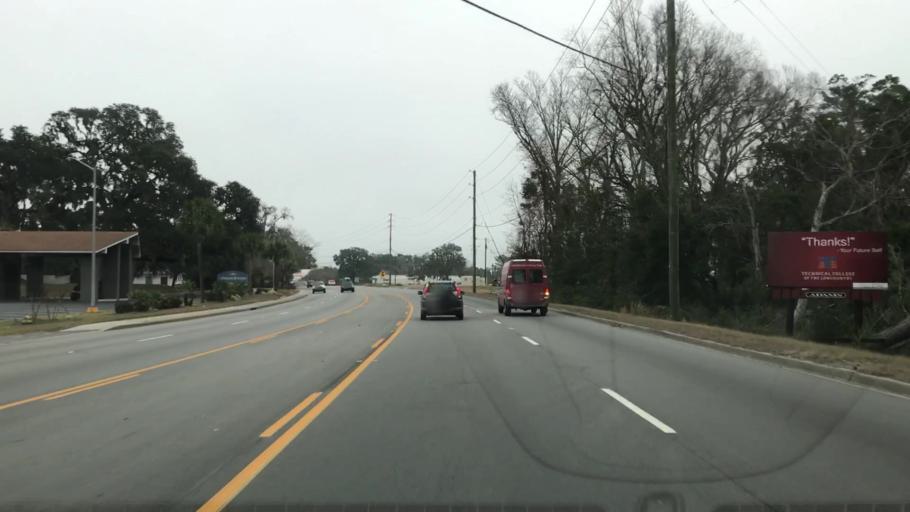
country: US
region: South Carolina
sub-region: Beaufort County
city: Burton
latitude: 32.4432
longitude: -80.7257
